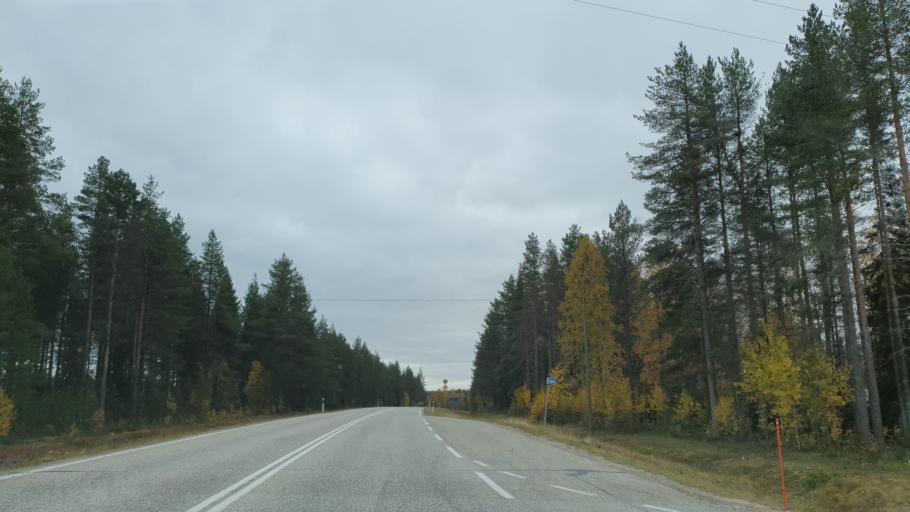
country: FI
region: Lapland
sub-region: Rovaniemi
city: Ranua
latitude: 65.6416
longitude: 26.7079
